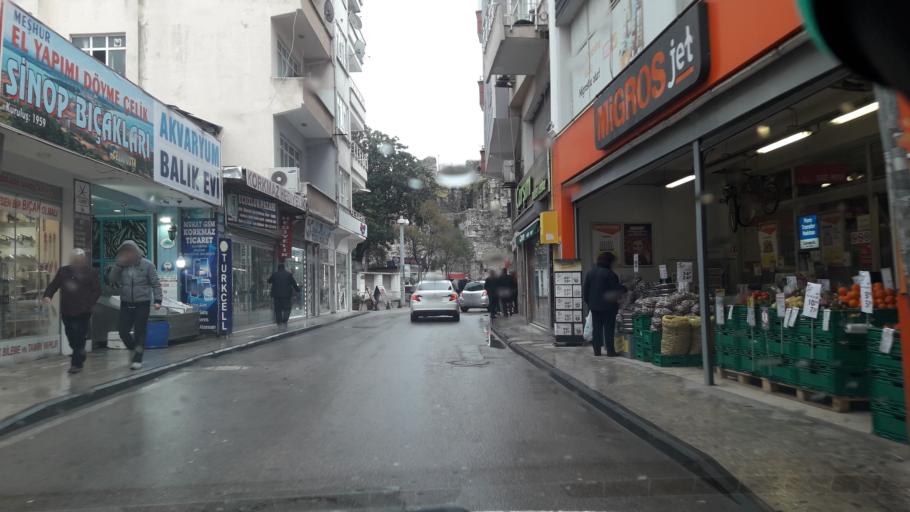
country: TR
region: Sinop
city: Sinop
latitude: 42.0245
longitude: 35.1497
